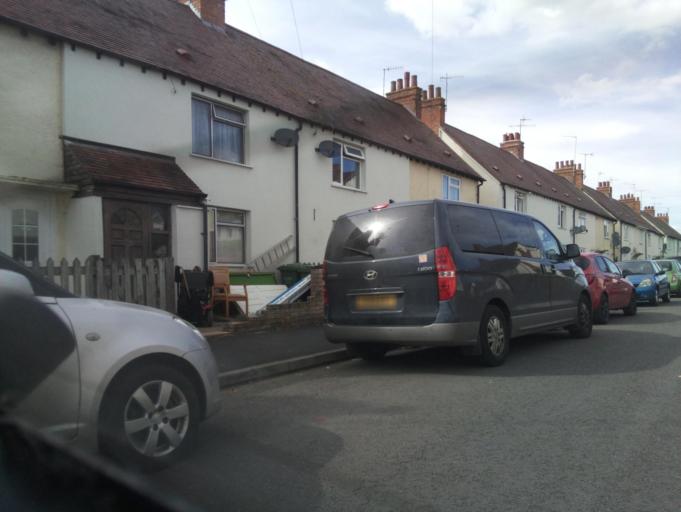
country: GB
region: England
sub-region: Worcestershire
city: Evesham
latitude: 52.0940
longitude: -1.9529
